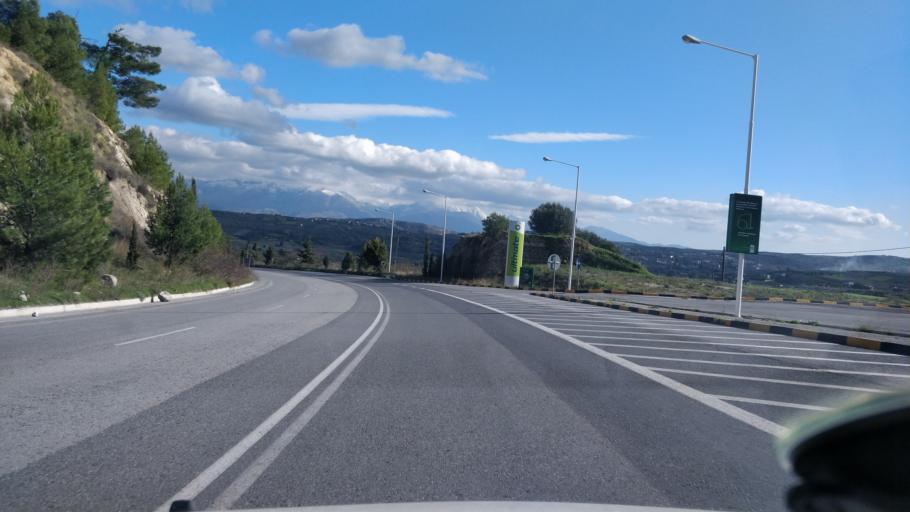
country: GR
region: Crete
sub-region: Nomos Irakleiou
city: Ano Arhanes
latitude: 35.2251
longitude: 25.1840
